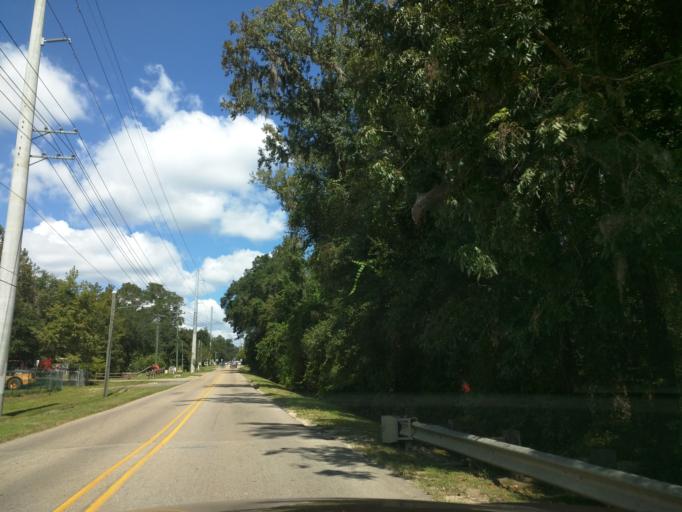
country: US
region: Florida
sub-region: Leon County
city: Tallahassee
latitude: 30.4555
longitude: -84.2224
